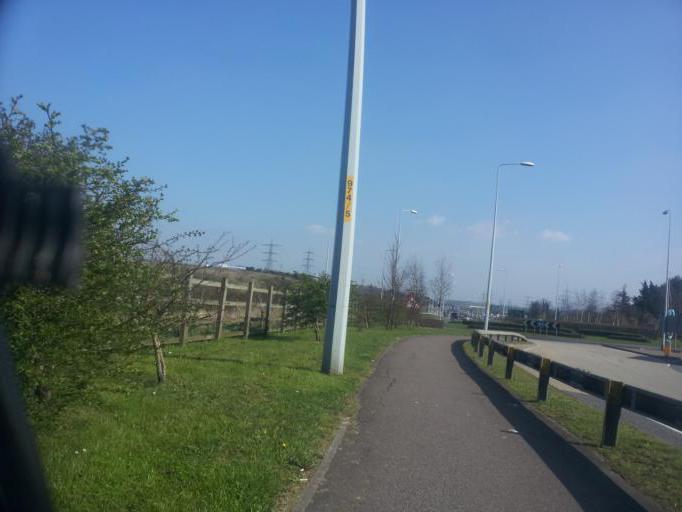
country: GB
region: England
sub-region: Kent
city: Swanscombe
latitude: 51.4318
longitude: 0.3204
